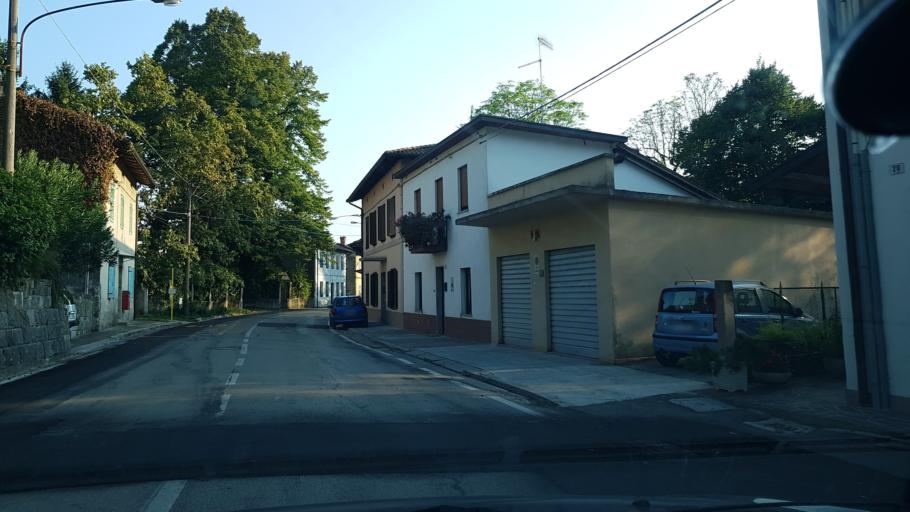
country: IT
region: Friuli Venezia Giulia
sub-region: Provincia di Gorizia
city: Gorizia
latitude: 45.9628
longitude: 13.6150
